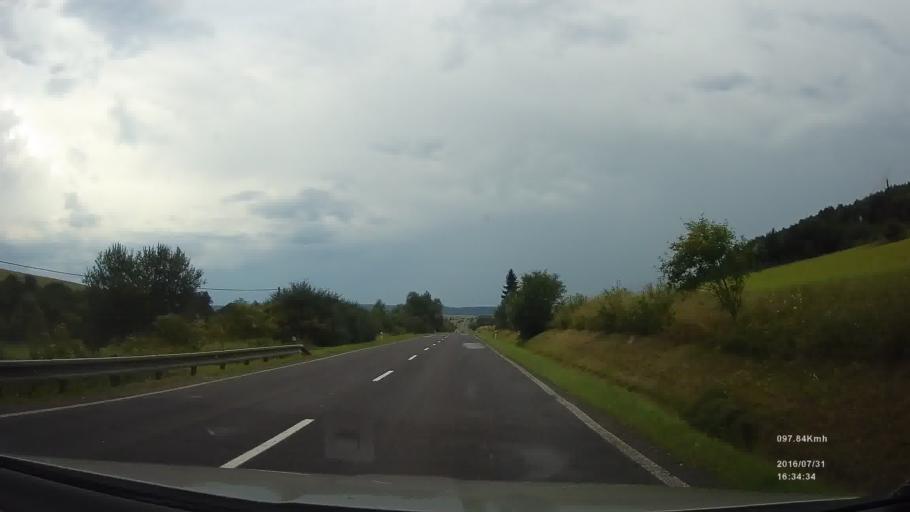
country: SK
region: Presovsky
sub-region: Okres Bardejov
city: Bardejov
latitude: 49.1669
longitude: 21.3107
